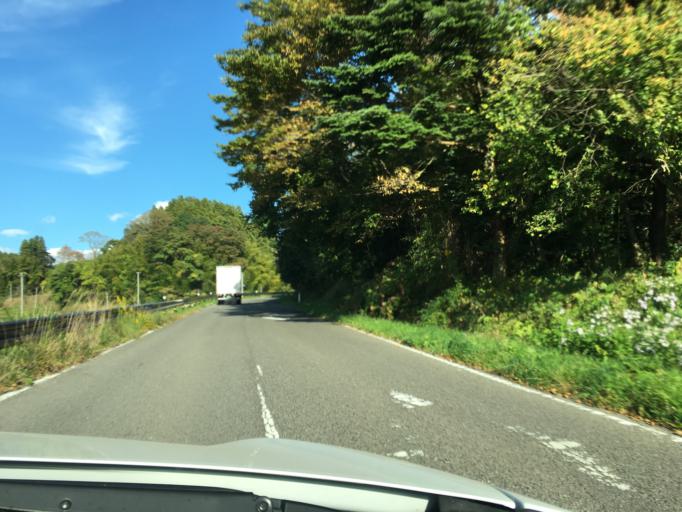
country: JP
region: Fukushima
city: Ishikawa
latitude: 37.2209
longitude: 140.4492
